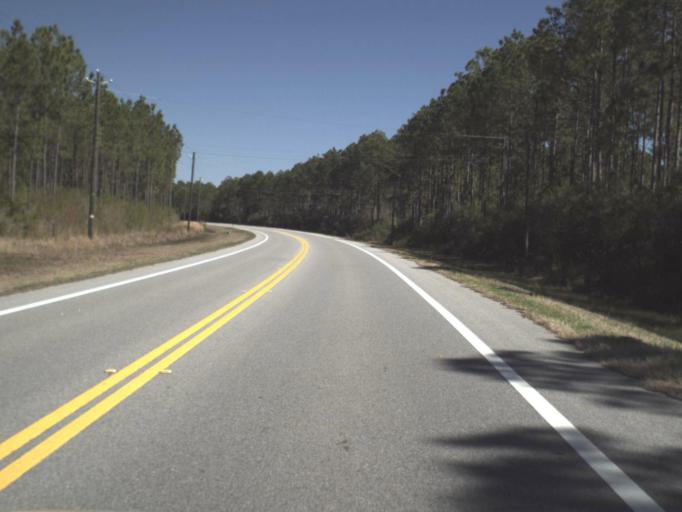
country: US
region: Florida
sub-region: Bay County
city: Laguna Beach
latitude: 30.2990
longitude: -85.8337
